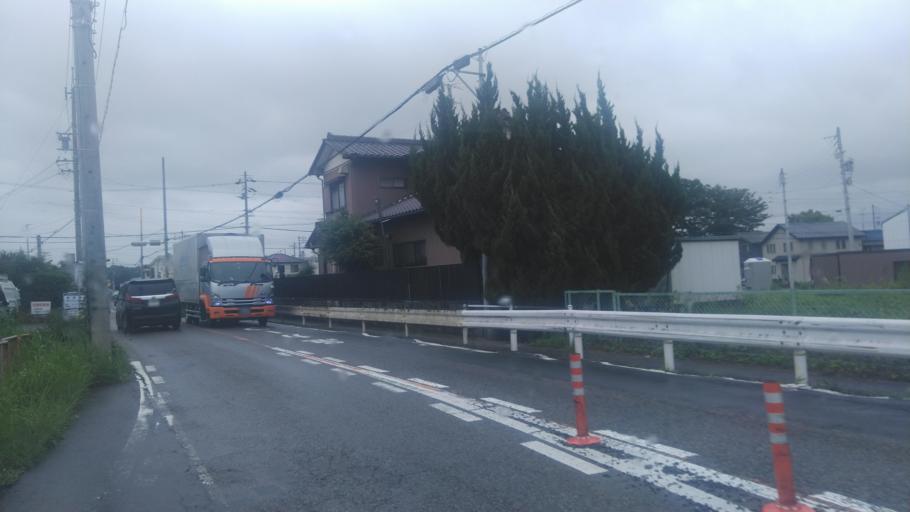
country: JP
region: Aichi
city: Kasugai
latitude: 35.2464
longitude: 137.0241
